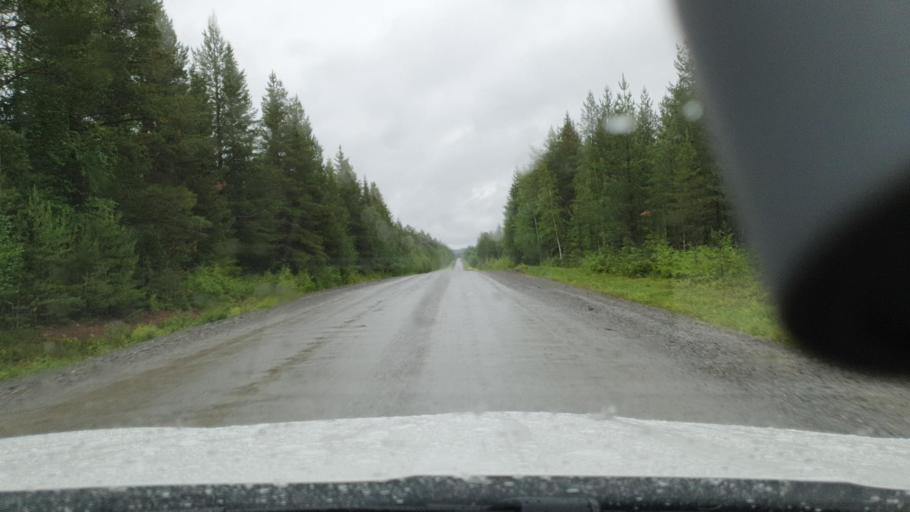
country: SE
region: Vaesterbotten
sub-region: Skelleftea Kommun
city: Burtraesk
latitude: 64.3790
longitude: 20.3456
